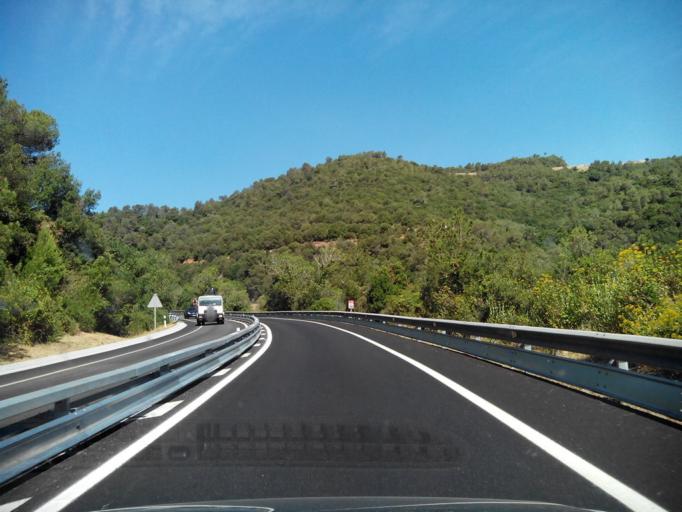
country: ES
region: Catalonia
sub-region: Provincia de Barcelona
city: Viladecavalls
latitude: 41.5838
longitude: 1.9509
